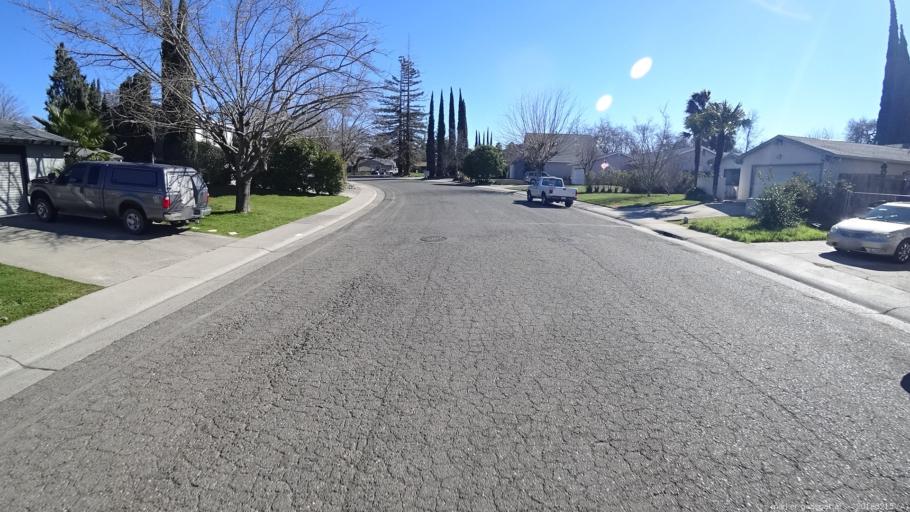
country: US
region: California
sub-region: Sacramento County
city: Antelope
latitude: 38.6933
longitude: -121.3330
